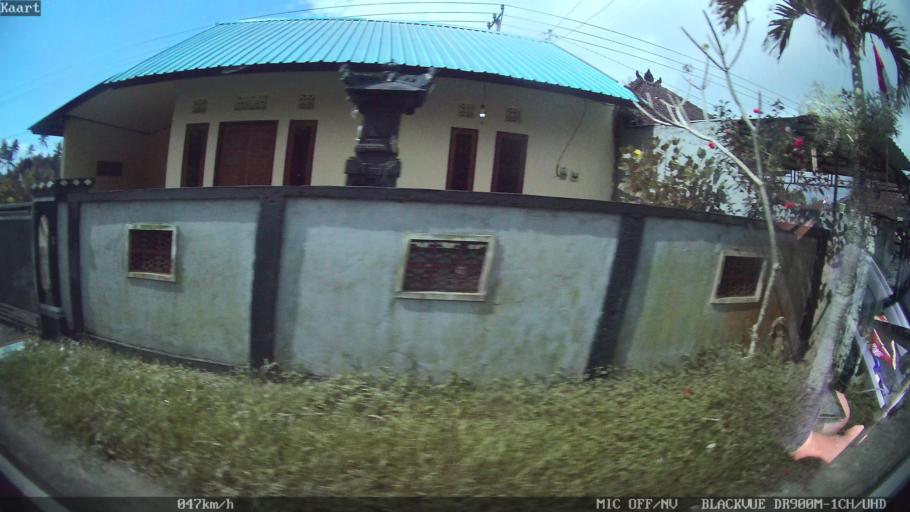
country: ID
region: Bali
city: Bantiran
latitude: -8.3031
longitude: 114.9810
